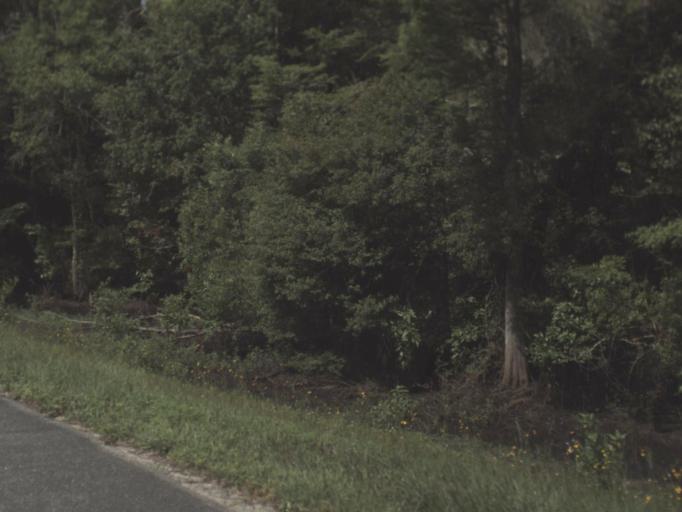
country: US
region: Florida
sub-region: Taylor County
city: Steinhatchee
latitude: 29.8340
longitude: -83.3134
